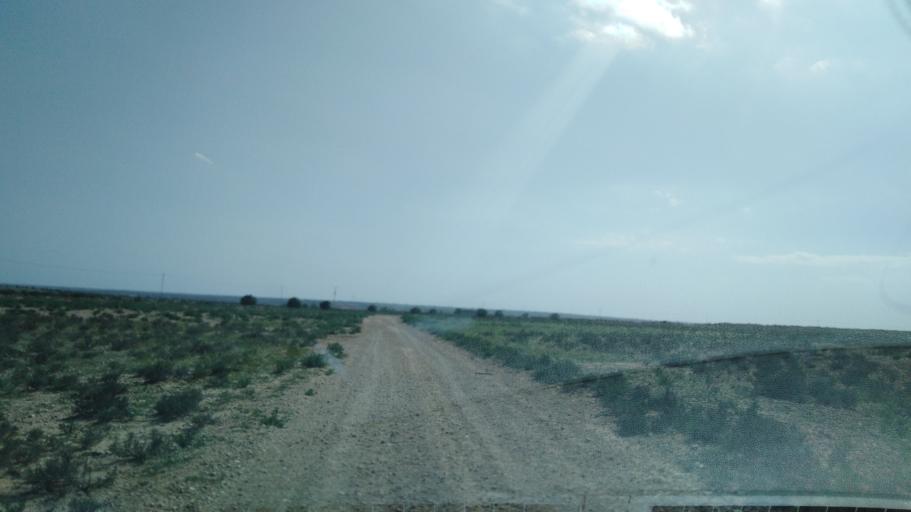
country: TN
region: Safaqis
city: Bi'r `Ali Bin Khalifah
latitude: 34.7978
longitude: 10.3749
